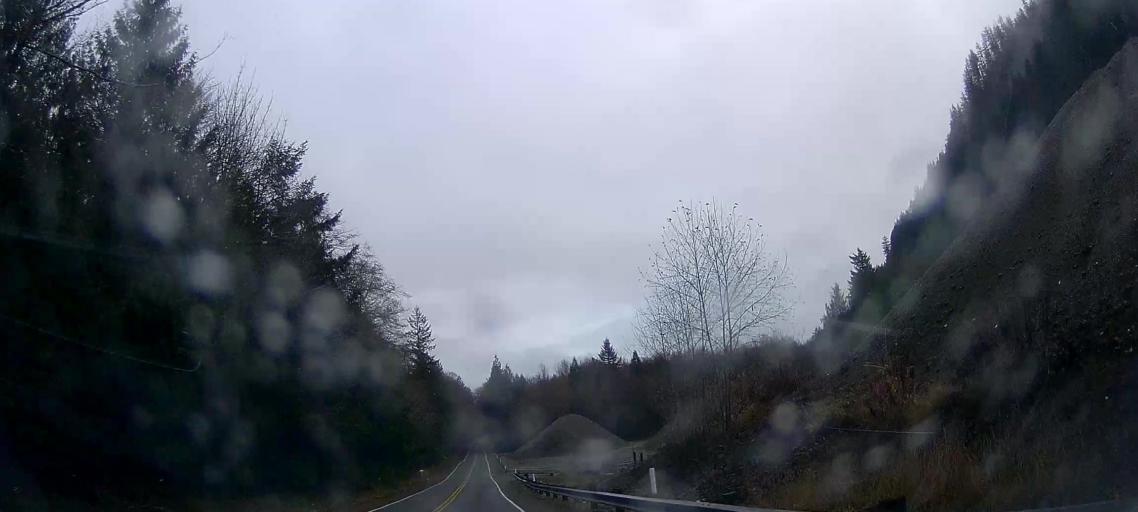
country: US
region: Washington
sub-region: Snohomish County
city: Darrington
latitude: 48.5316
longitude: -121.7975
